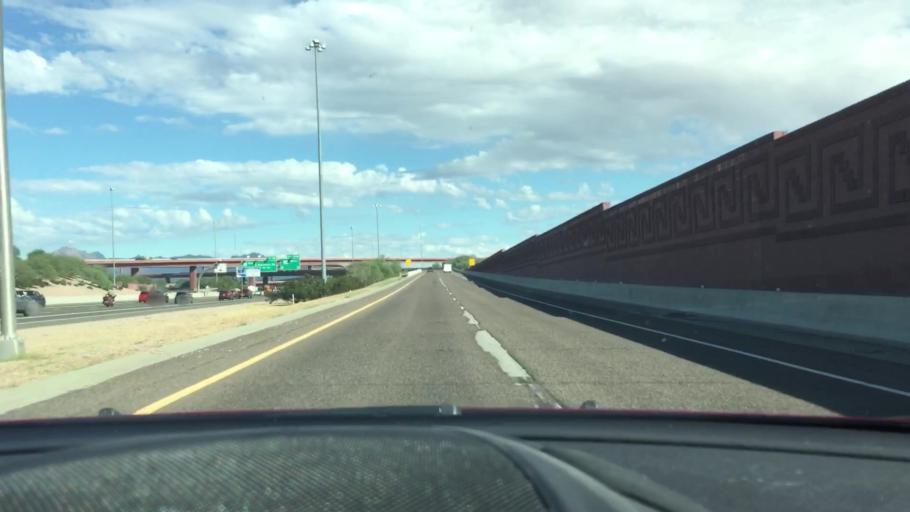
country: US
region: Arizona
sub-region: Pinal County
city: Apache Junction
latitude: 33.3863
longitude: -111.6560
